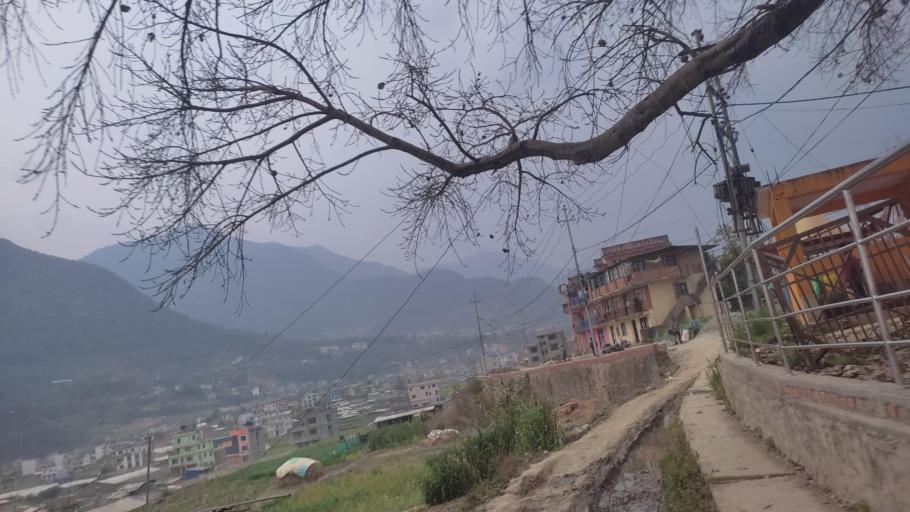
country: NP
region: Central Region
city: Kirtipur
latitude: 27.6631
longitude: 85.2725
